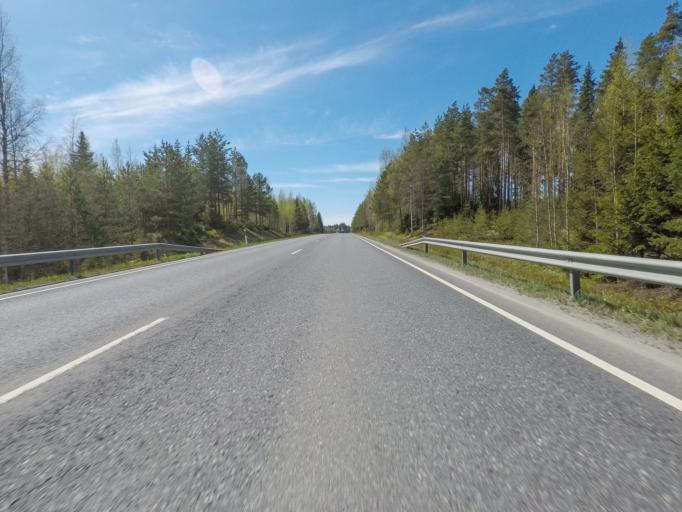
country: FI
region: Haeme
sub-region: Forssa
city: Humppila
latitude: 60.9682
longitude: 23.3972
